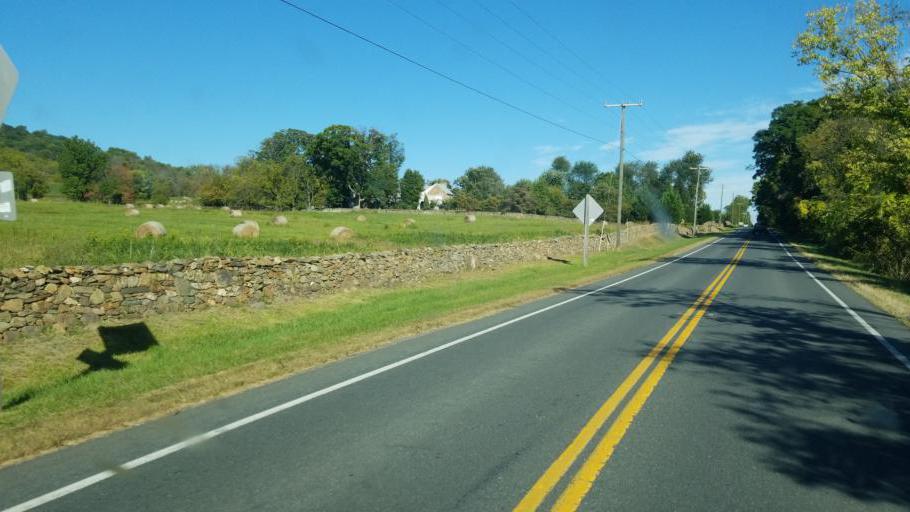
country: US
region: Virginia
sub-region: Warren County
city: Shenandoah Farms
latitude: 39.0019
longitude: -77.9390
